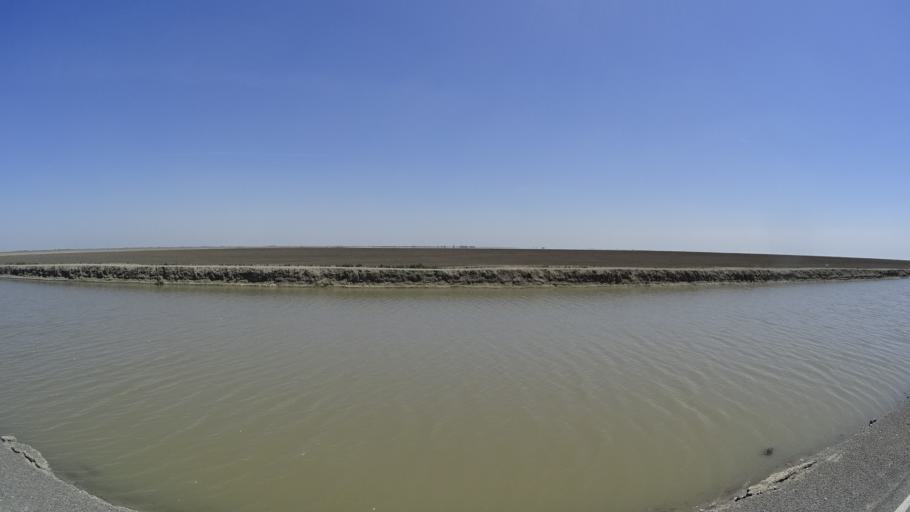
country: US
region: California
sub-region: Kings County
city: Corcoran
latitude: 36.0380
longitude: -119.6429
